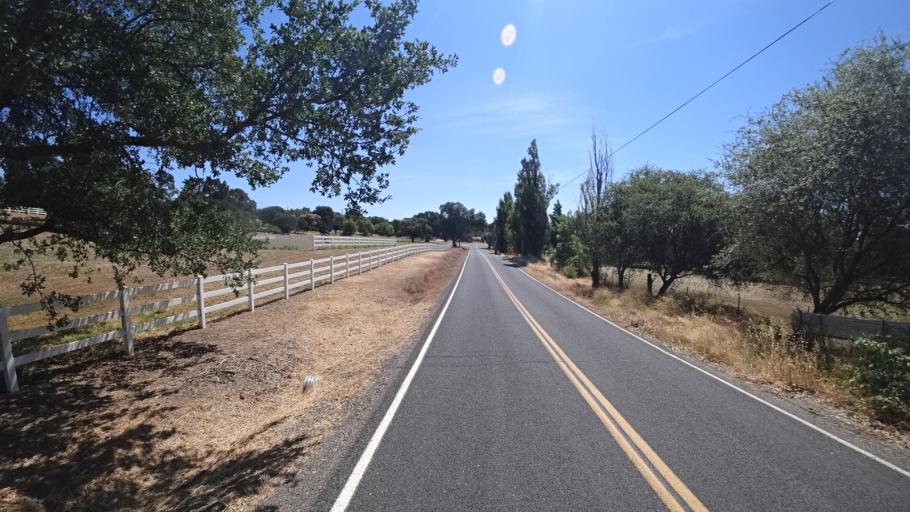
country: US
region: California
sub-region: Calaveras County
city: Rancho Calaveras
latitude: 38.1484
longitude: -120.9353
